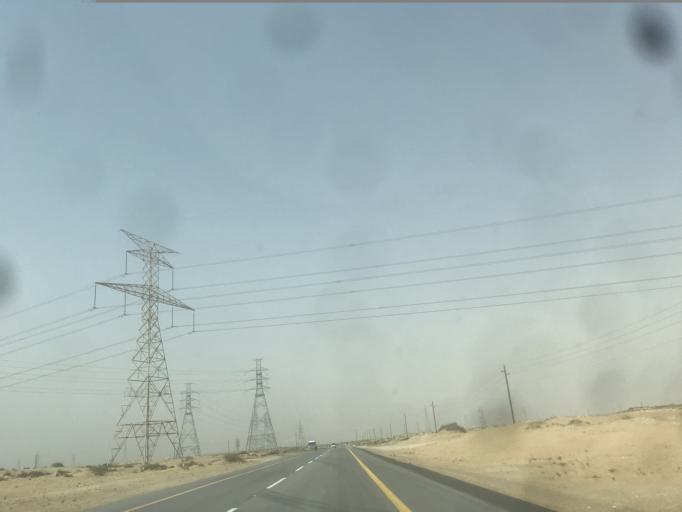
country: SA
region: Eastern Province
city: Abqaiq
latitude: 25.9383
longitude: 49.7206
